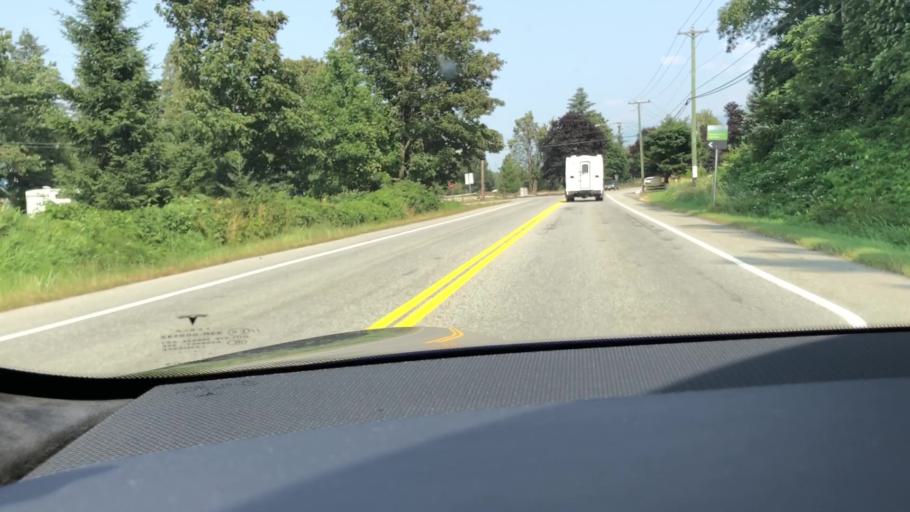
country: CA
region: British Columbia
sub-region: Fraser Valley Regional District
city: Chilliwack
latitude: 49.0889
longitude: -122.0189
